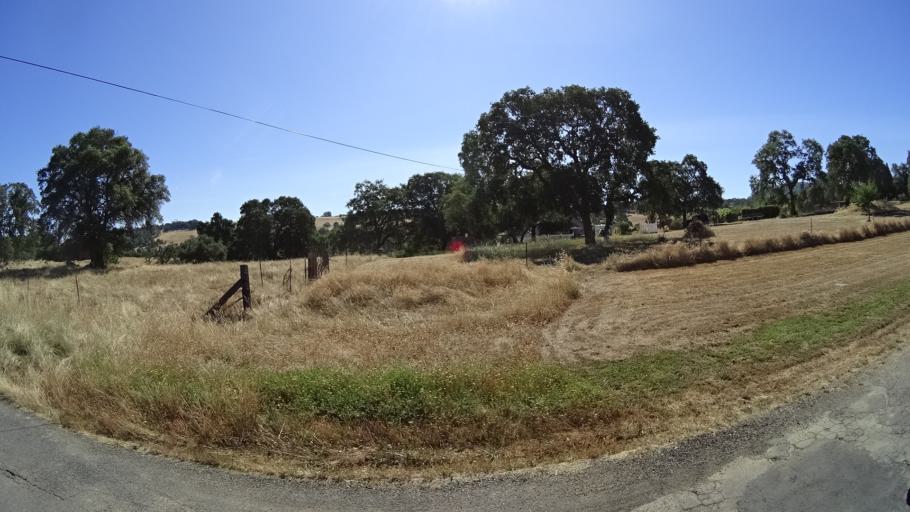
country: US
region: California
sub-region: Amador County
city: Jackson
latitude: 38.2645
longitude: -120.7641
